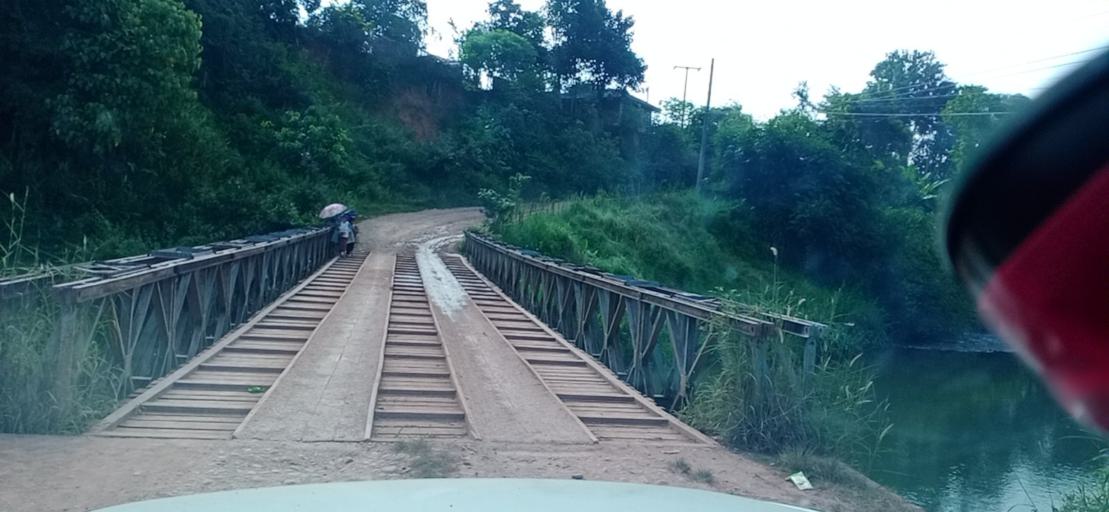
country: TH
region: Changwat Bueng Kan
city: Pak Khat
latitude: 18.6798
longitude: 103.1890
